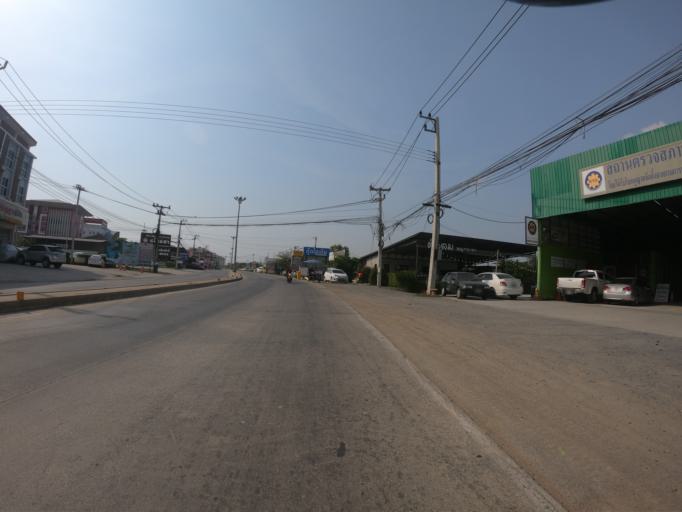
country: TH
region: Phra Nakhon Si Ayutthaya
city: Phra Nakhon Si Ayutthaya
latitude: 14.3399
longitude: 100.5963
